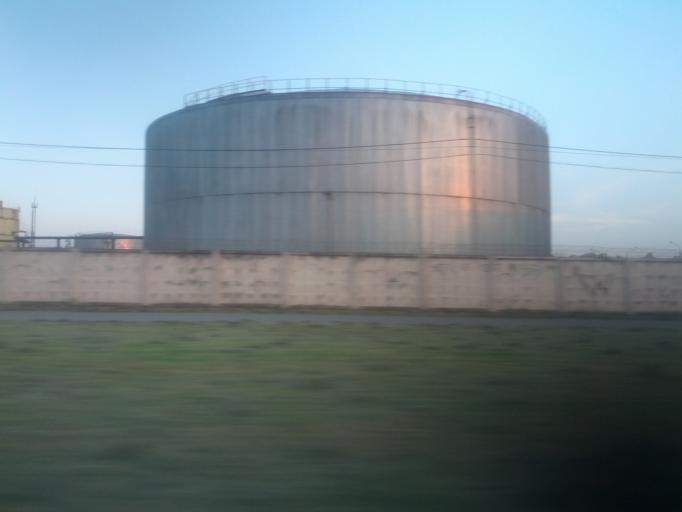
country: RU
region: St.-Petersburg
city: Staraya Derevnya
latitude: 59.9971
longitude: 30.2397
